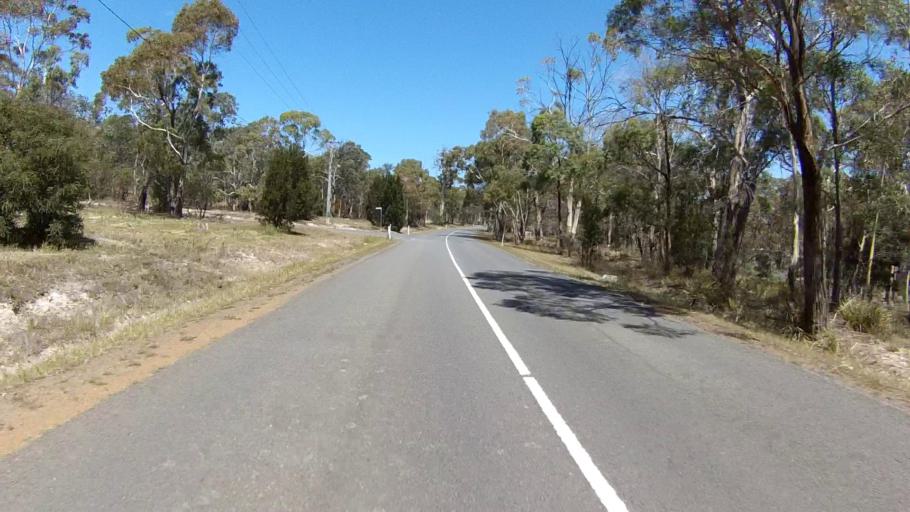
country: AU
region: Tasmania
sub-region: Clarence
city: Sandford
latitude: -42.9702
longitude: 147.4798
